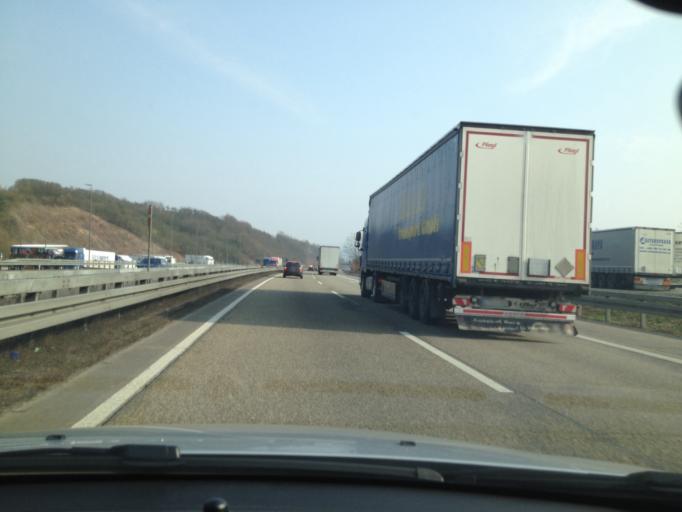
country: DE
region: Hesse
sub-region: Regierungsbezirk Giessen
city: Wetzlar
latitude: 50.5922
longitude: 8.5175
